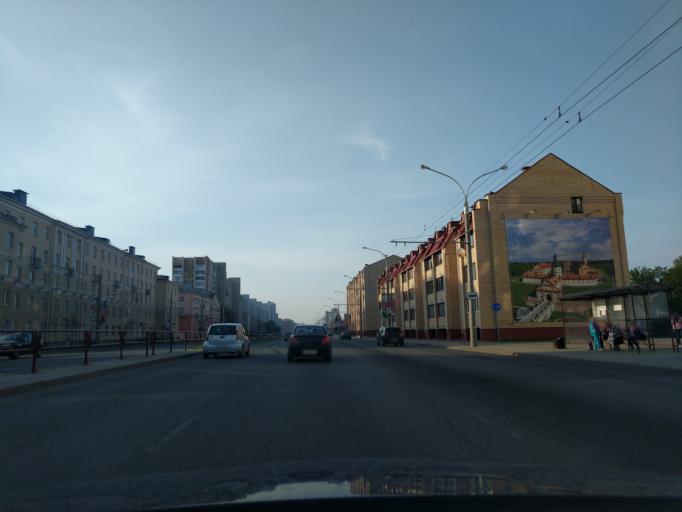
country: BY
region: Minsk
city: Minsk
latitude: 53.8643
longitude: 27.5712
